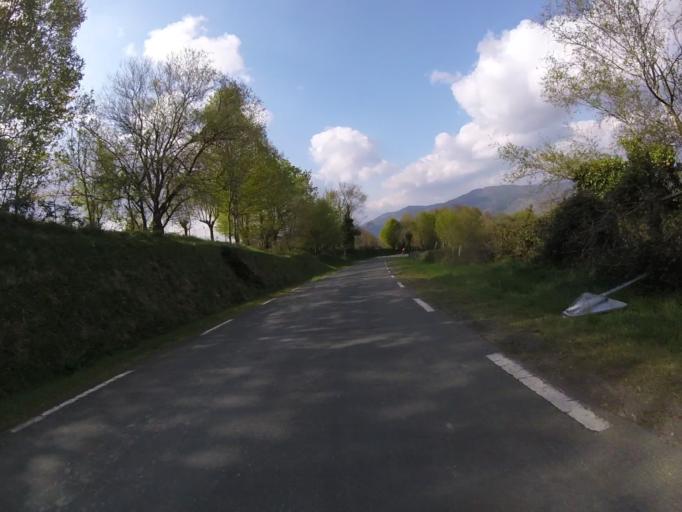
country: ES
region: Basque Country
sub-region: Provincia de Guipuzcoa
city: Azkoitia
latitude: 43.2080
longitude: -2.3348
